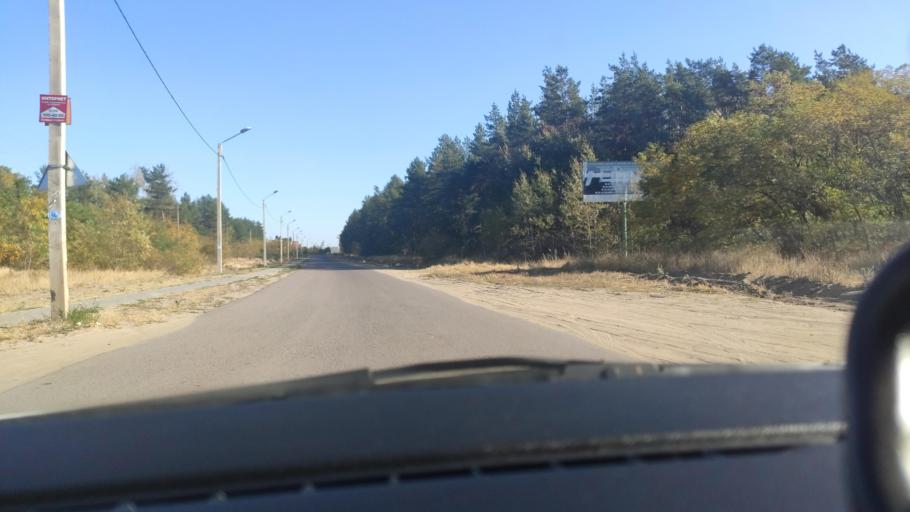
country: RU
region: Voronezj
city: Pridonskoy
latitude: 51.6249
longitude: 39.0830
